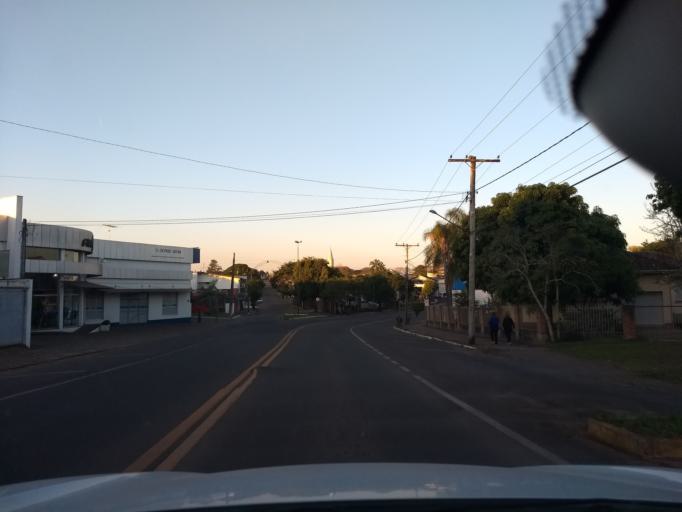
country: BR
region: Rio Grande do Sul
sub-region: Santa Cruz Do Sul
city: Santa Cruz do Sul
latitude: -29.7173
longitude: -52.5092
